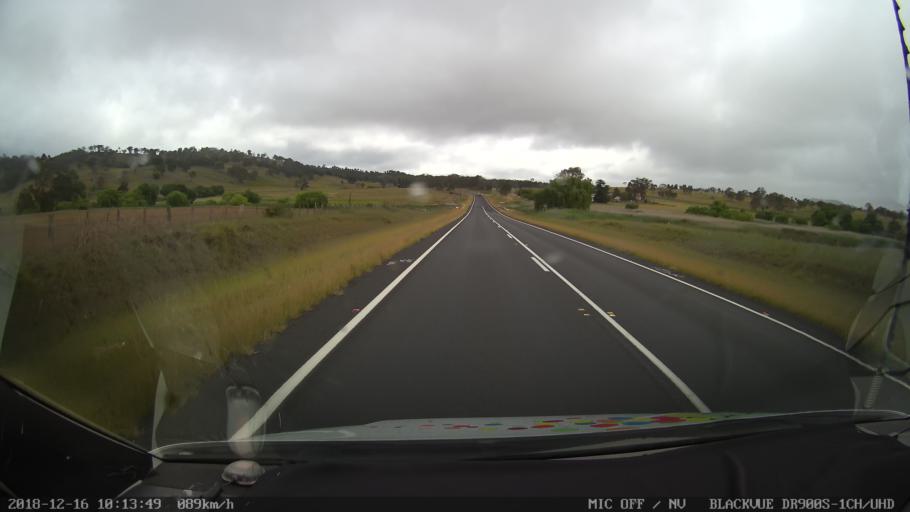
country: AU
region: New South Wales
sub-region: Glen Innes Severn
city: Glen Innes
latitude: -29.2936
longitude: 151.9570
